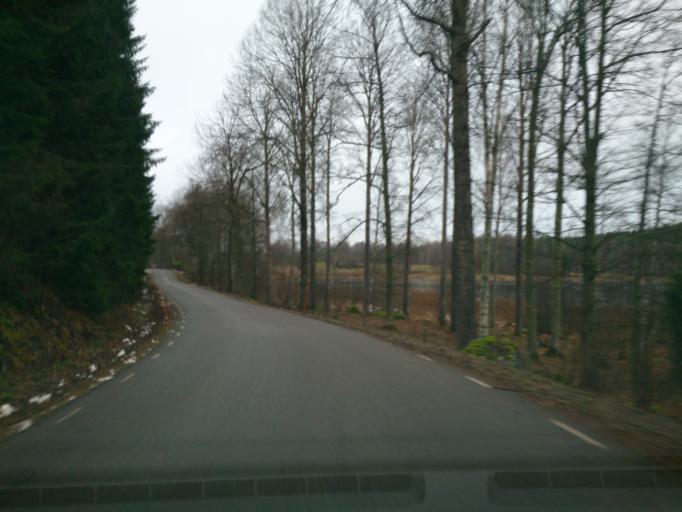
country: SE
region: OEstergoetland
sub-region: Atvidabergs Kommun
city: Atvidaberg
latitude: 58.2748
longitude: 16.1496
